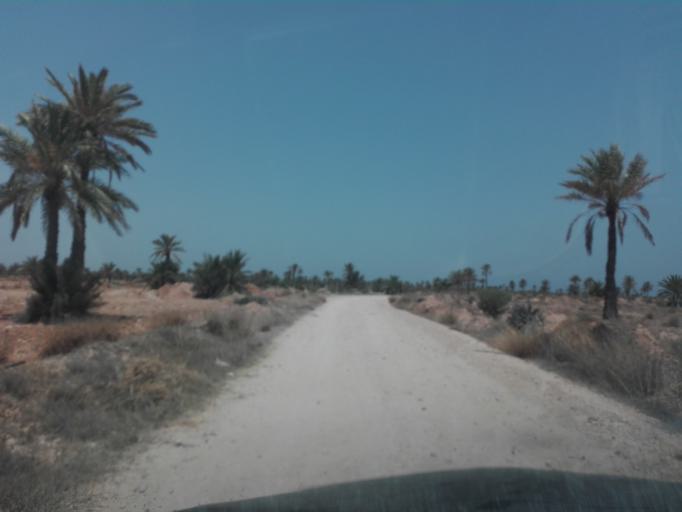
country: TN
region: Safaqis
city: Al Qarmadah
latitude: 34.6607
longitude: 11.0991
